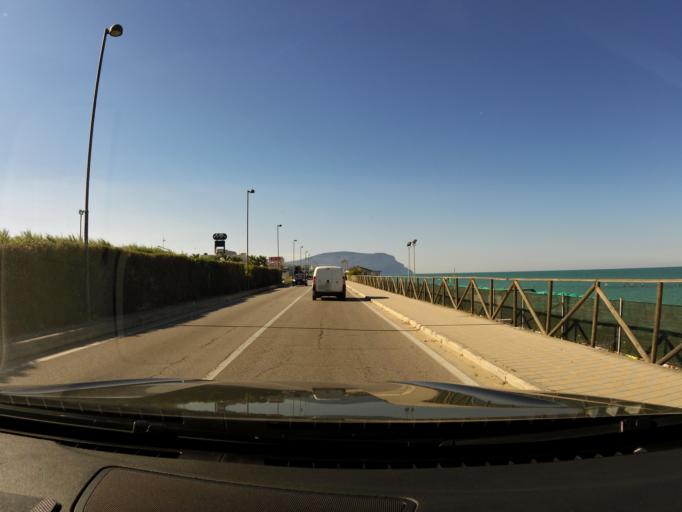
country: IT
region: The Marches
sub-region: Provincia di Macerata
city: Porto Recanati
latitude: 43.4518
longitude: 13.6539
